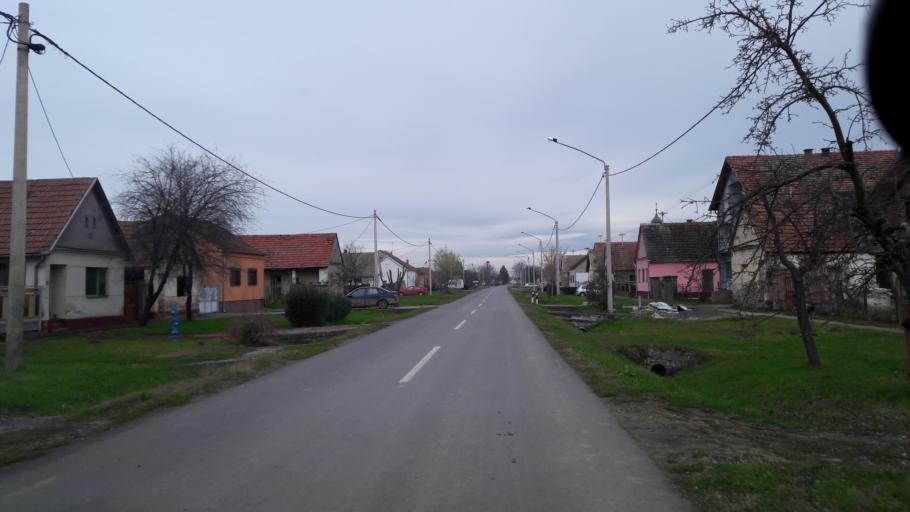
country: HR
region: Osjecko-Baranjska
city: Vladislavci
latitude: 45.4489
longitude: 18.5601
